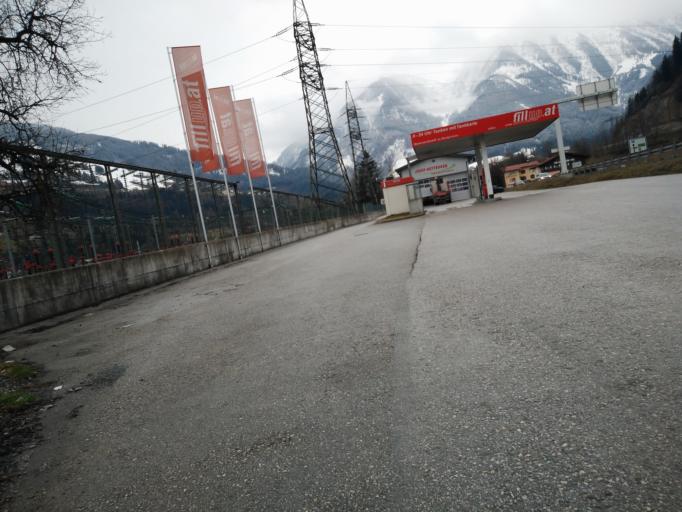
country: AT
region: Salzburg
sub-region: Politischer Bezirk Sankt Johann im Pongau
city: Sankt Johann im Pongau
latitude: 47.3372
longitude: 13.1896
